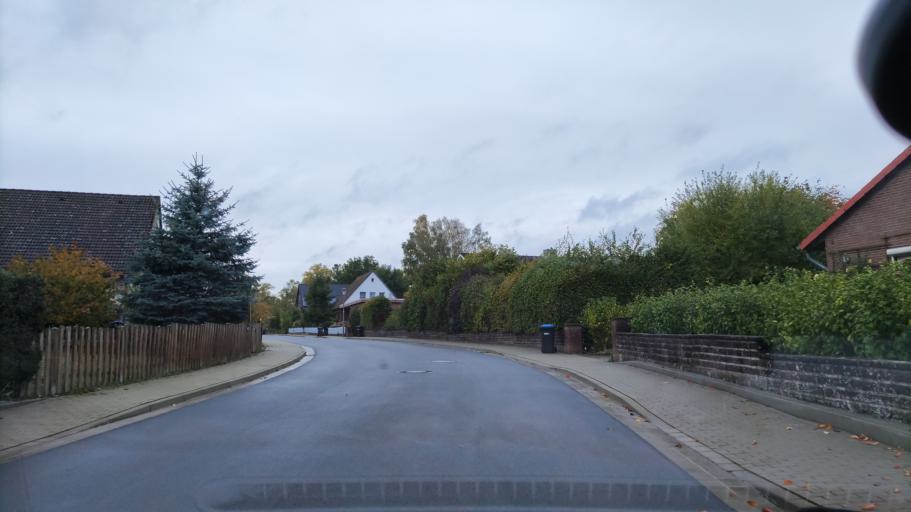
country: DE
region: Lower Saxony
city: Deutsch Evern
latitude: 53.1985
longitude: 10.4416
